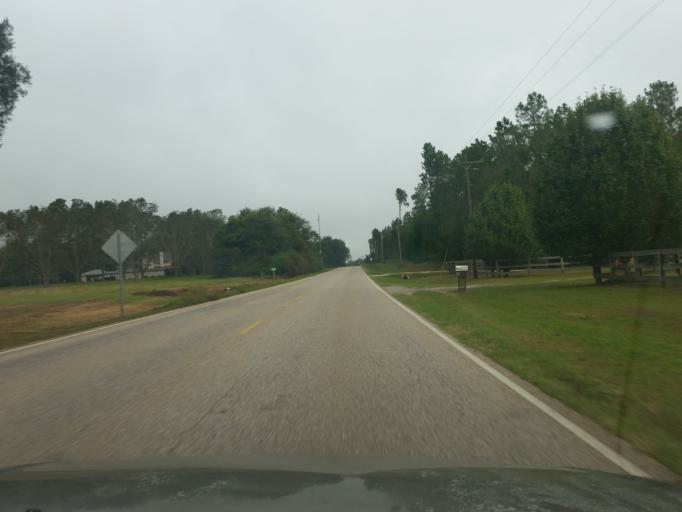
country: US
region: Florida
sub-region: Escambia County
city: Cantonment
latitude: 30.6348
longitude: -87.4404
